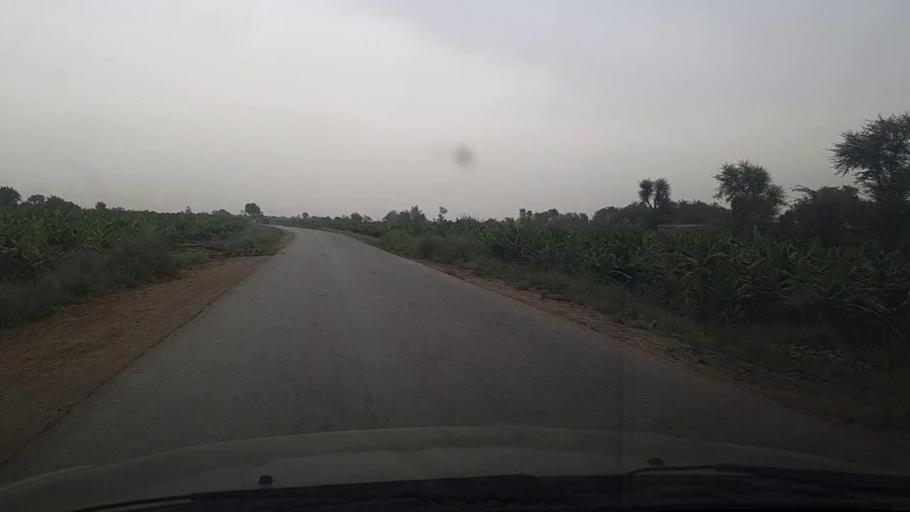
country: PK
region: Sindh
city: Daur
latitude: 26.4006
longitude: 68.2189
